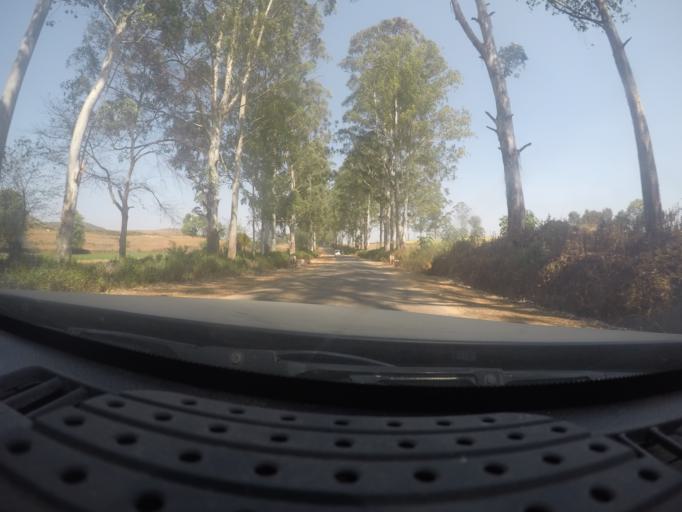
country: MM
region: Shan
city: Taunggyi
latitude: 20.8597
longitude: 96.5896
